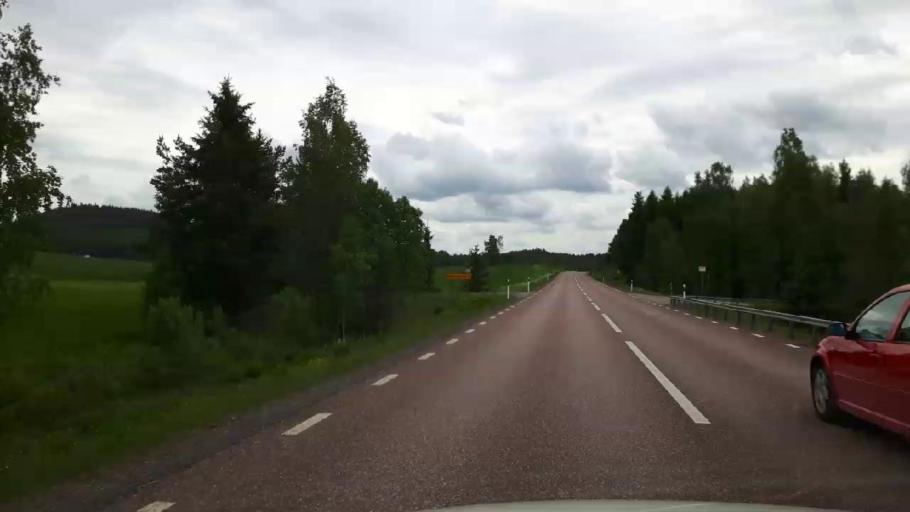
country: SE
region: Dalarna
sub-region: Hedemora Kommun
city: Brunna
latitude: 60.2184
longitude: 15.9908
